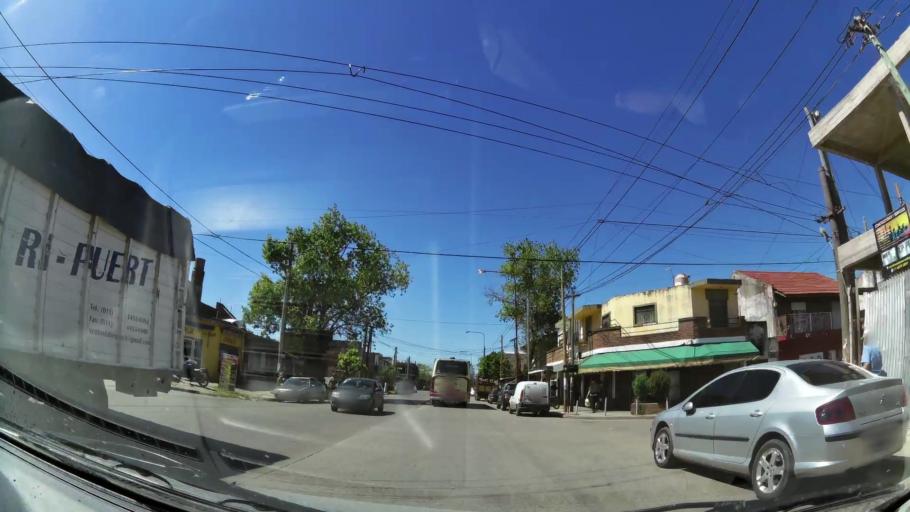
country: AR
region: Buenos Aires
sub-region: Partido de Quilmes
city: Quilmes
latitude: -34.7300
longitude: -58.3044
